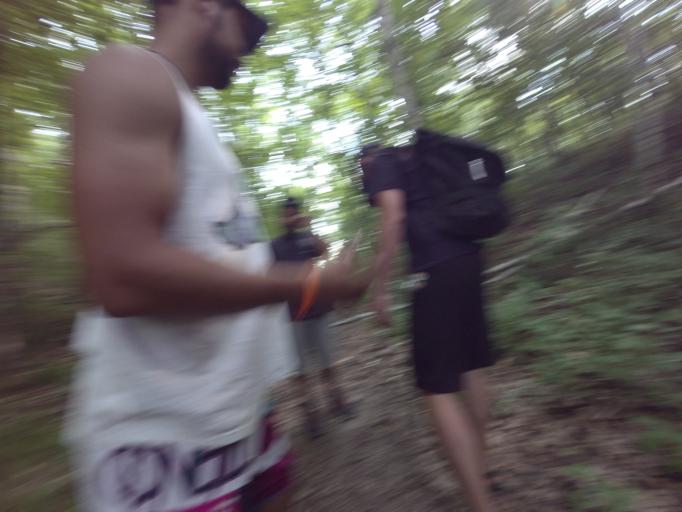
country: US
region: Wisconsin
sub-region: Washington County
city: Kewaskum
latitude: 43.5845
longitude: -88.1791
